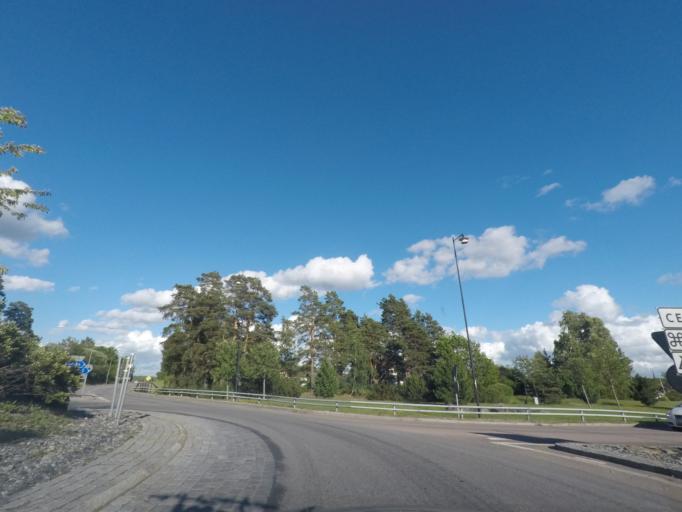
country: SE
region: Vaestmanland
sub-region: Arboga Kommun
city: Arboga
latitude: 59.4044
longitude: 15.8315
